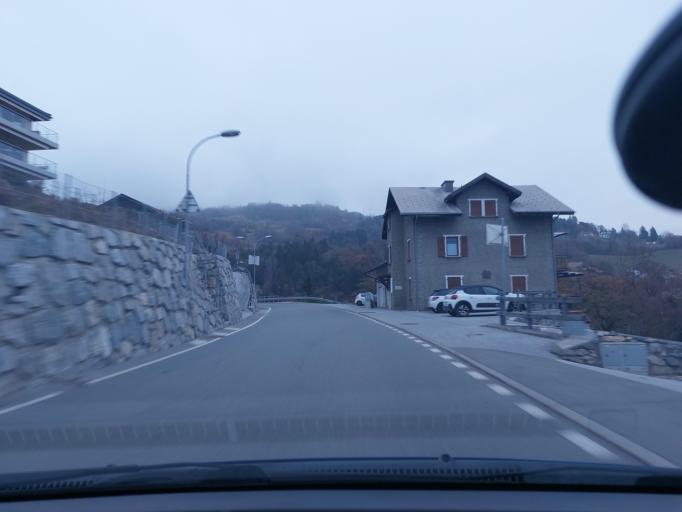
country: CH
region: Valais
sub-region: Sion District
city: Grimisuat
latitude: 46.2611
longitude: 7.3691
